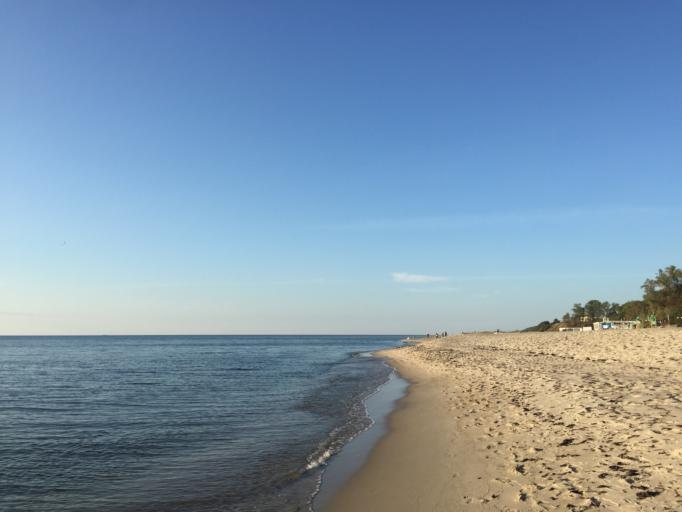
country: RU
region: Kaliningrad
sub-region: Gorod Kaliningrad
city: Yantarnyy
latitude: 54.8656
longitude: 19.9324
